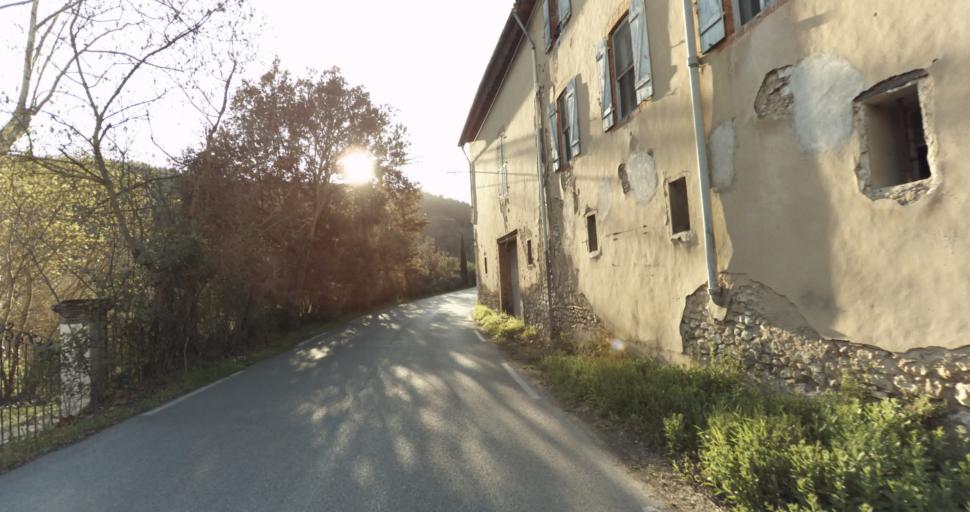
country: FR
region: Provence-Alpes-Cote d'Azur
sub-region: Departement des Bouches-du-Rhone
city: Ventabren
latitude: 43.5155
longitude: 5.3070
